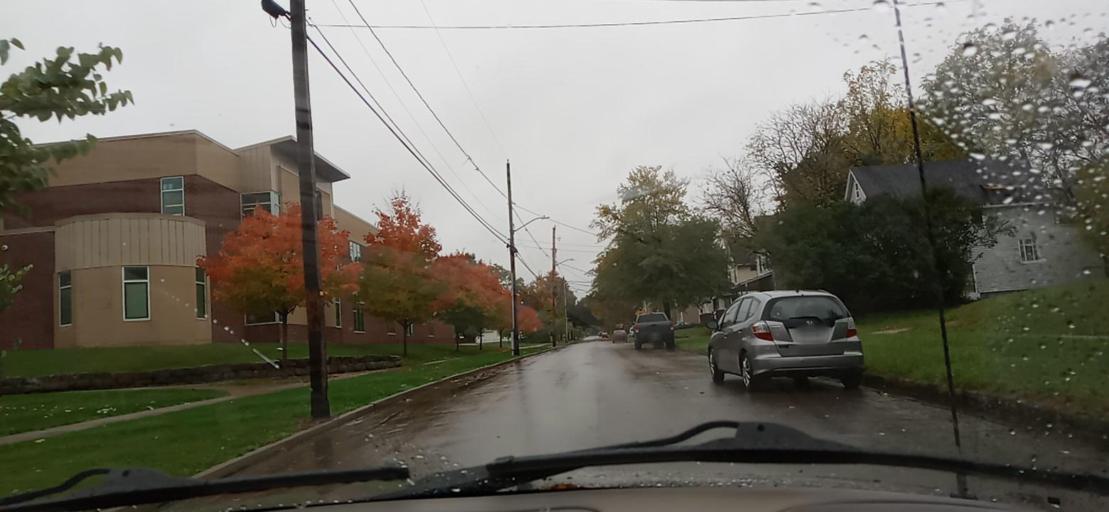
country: US
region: Ohio
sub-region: Summit County
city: Akron
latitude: 41.0674
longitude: -81.5149
